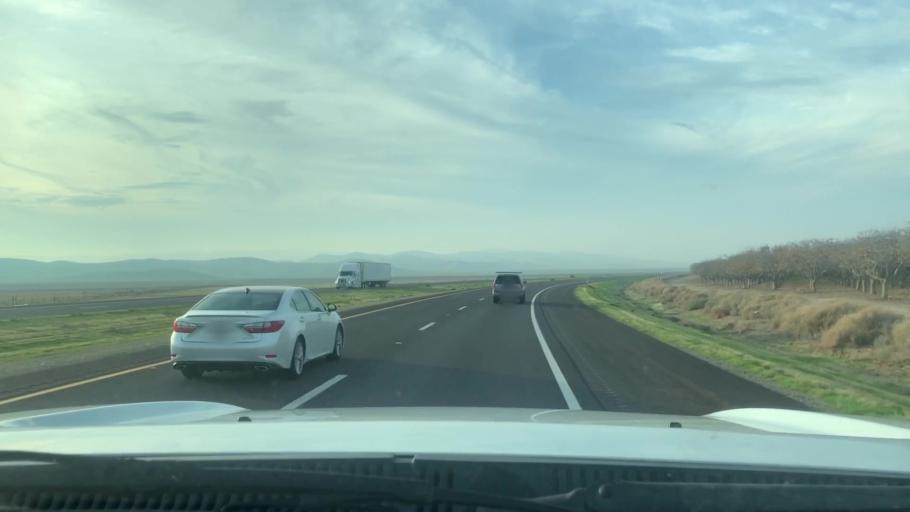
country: US
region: California
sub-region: Kern County
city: Lost Hills
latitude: 35.6145
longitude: -119.9644
